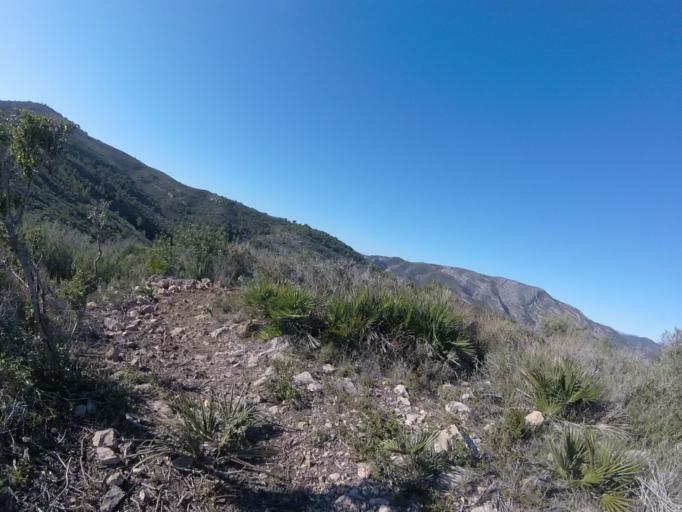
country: ES
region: Valencia
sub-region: Provincia de Castello
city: Orpesa/Oropesa del Mar
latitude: 40.1111
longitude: 0.1197
